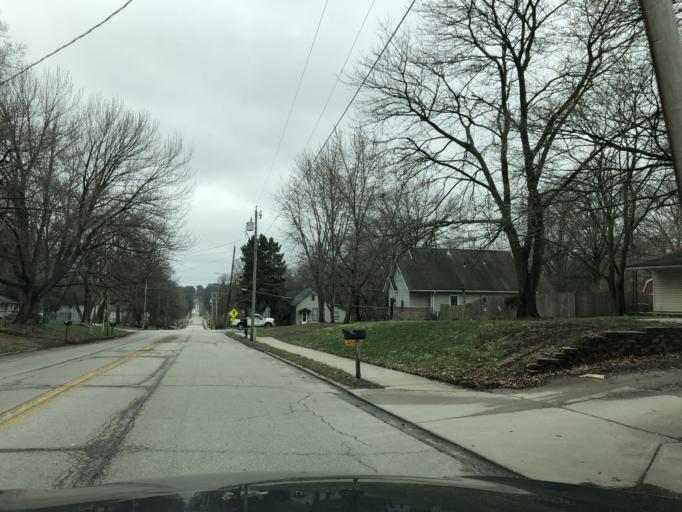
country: US
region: Kansas
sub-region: Leavenworth County
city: Leavenworth
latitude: 39.2929
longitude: -94.9185
